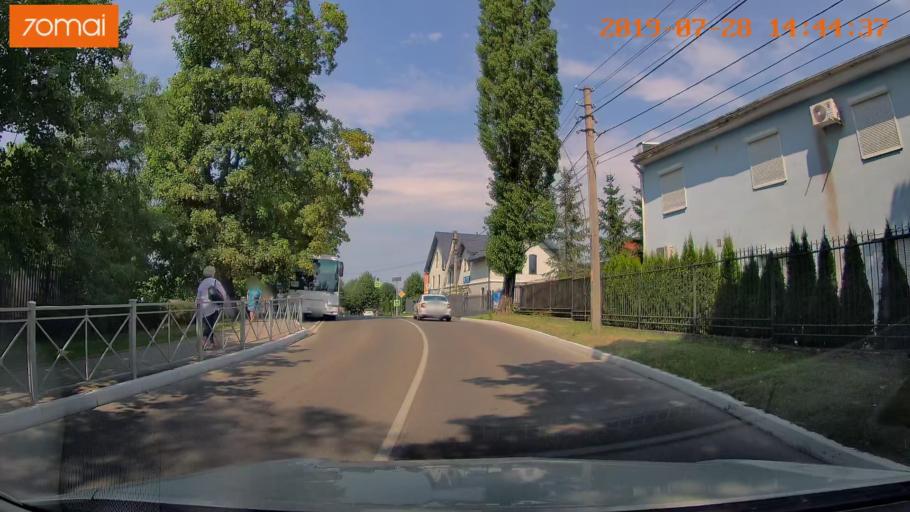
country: RU
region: Kaliningrad
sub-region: Gorod Kaliningrad
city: Yantarnyy
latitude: 54.8683
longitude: 19.9388
